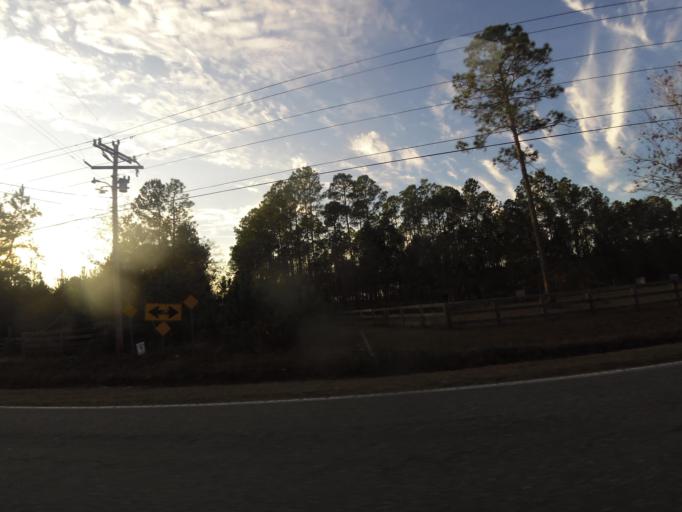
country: US
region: Florida
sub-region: Duval County
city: Baldwin
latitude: 30.1577
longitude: -82.0008
